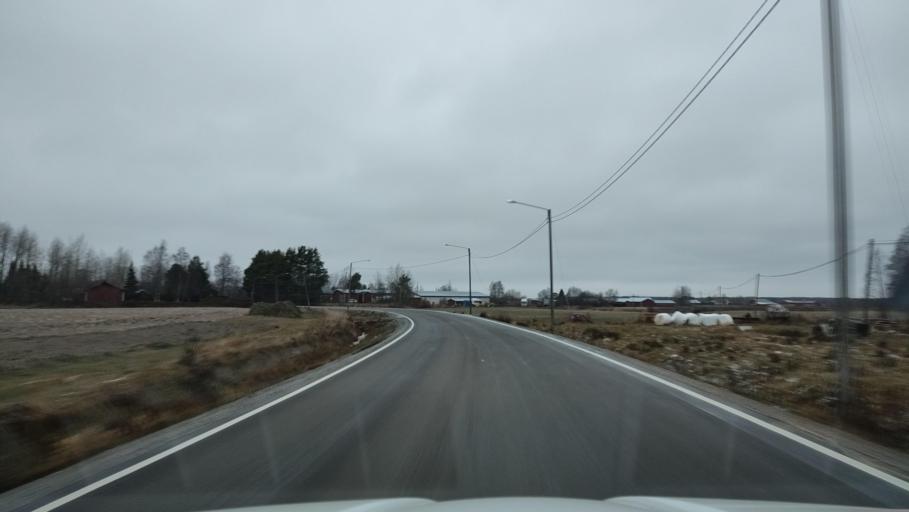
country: FI
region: Southern Ostrobothnia
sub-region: Suupohja
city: Karijoki
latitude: 62.2485
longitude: 21.5540
